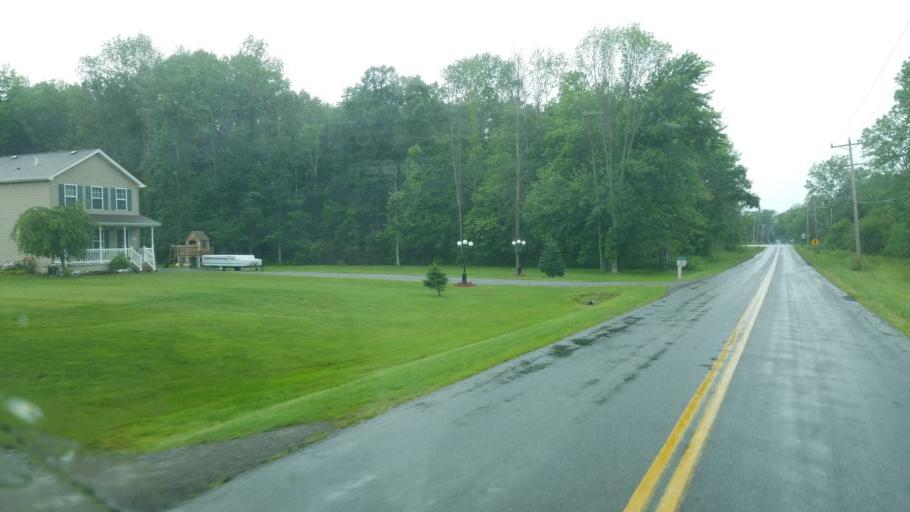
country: US
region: New York
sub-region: Niagara County
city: Ransomville
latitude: 43.2421
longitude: -78.8956
